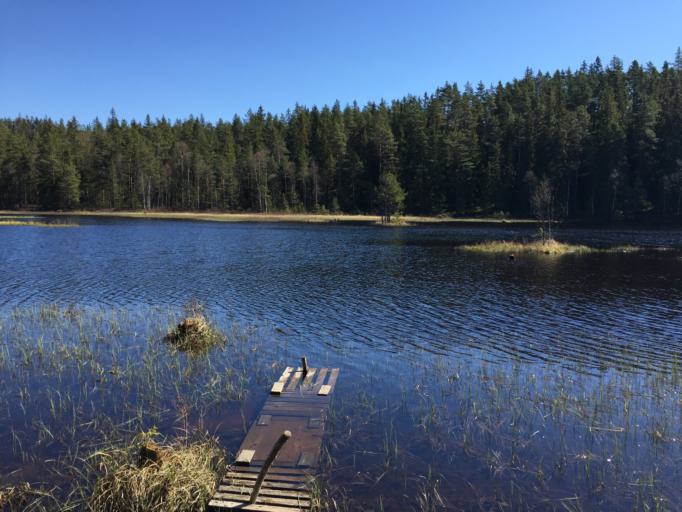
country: SE
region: Joenkoeping
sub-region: Vaggeryds Kommun
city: Skillingaryd
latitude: 57.4619
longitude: 14.0061
